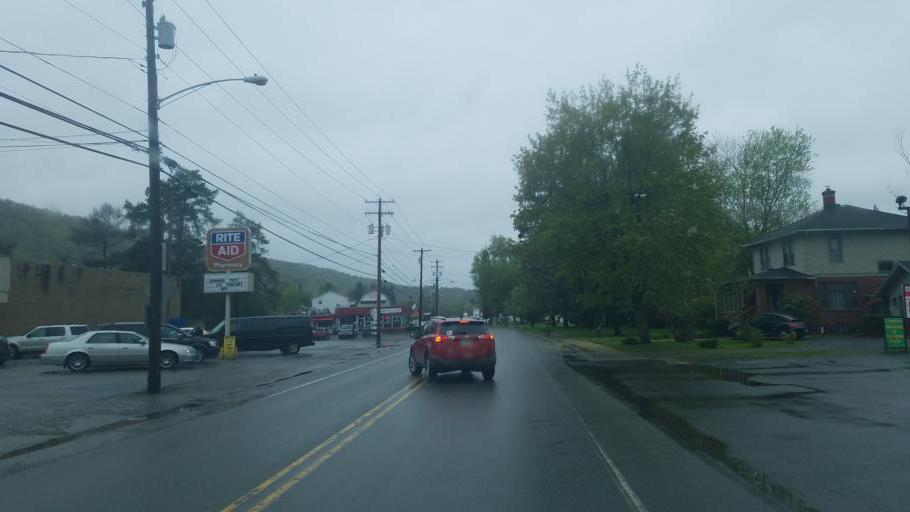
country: US
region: Pennsylvania
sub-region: Potter County
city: Coudersport
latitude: 41.7673
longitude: -78.0297
